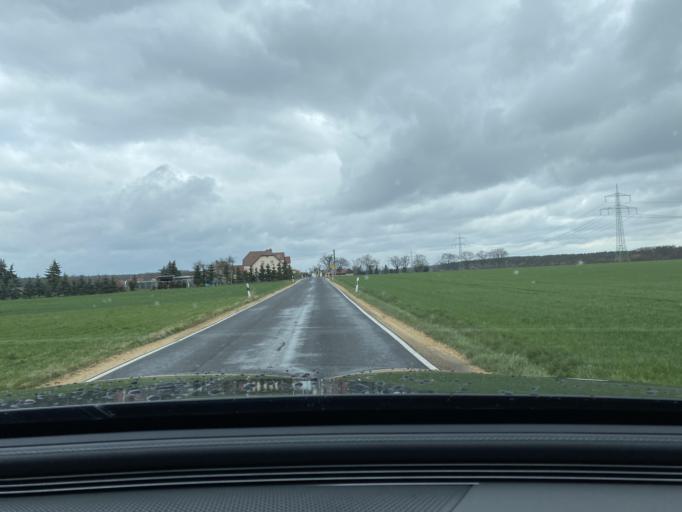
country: DE
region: Saxony
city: Radibor
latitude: 51.2688
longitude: 14.4303
